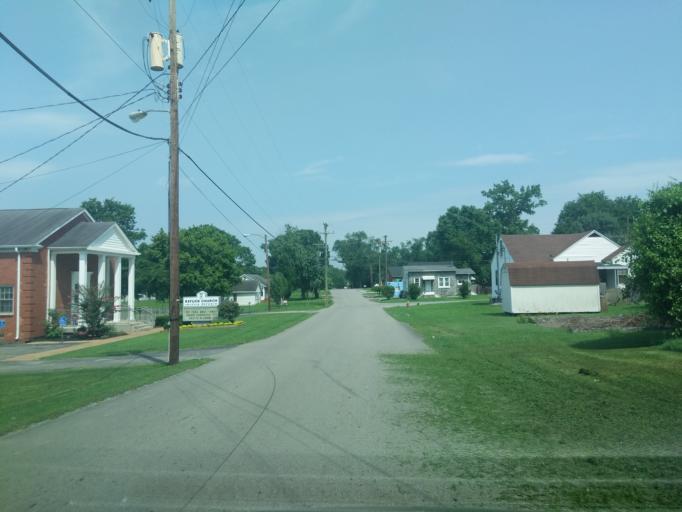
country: US
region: Tennessee
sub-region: Davidson County
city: Lakewood
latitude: 36.2707
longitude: -86.6669
